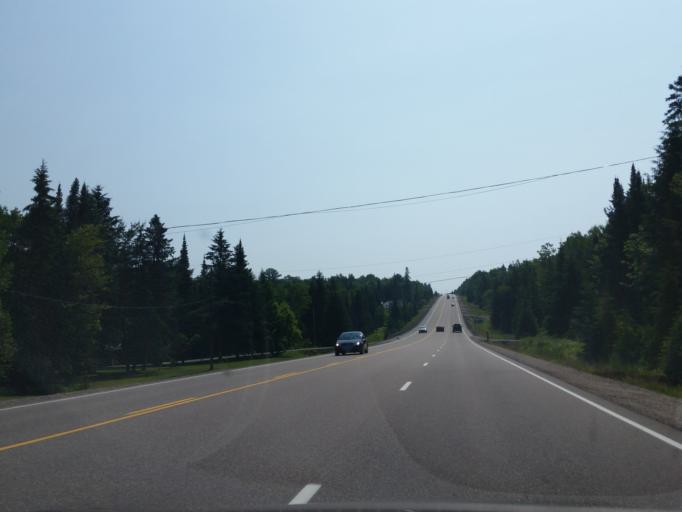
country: CA
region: Ontario
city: Mattawa
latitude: 46.3114
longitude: -78.6685
